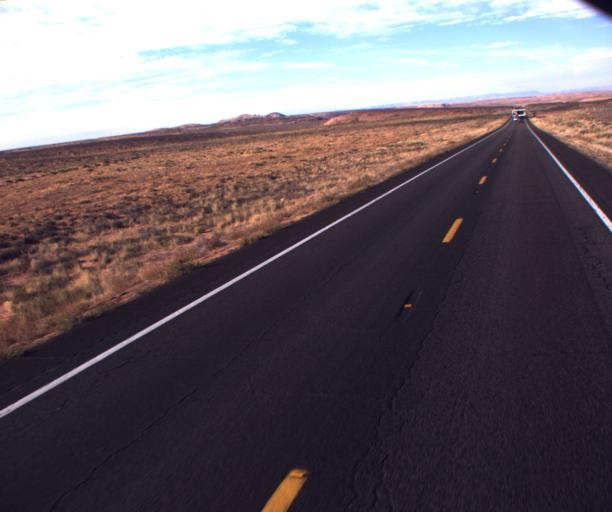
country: US
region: Arizona
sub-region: Apache County
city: Many Farms
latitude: 36.9382
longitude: -109.5528
